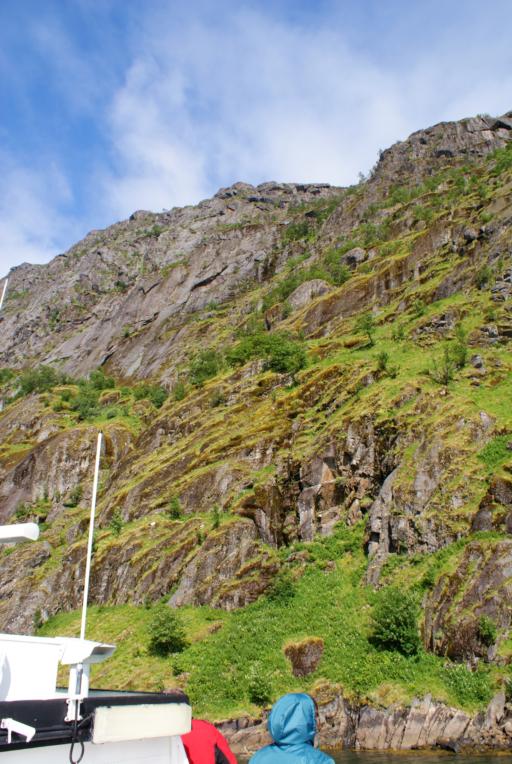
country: NO
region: Nordland
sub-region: Hadsel
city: Stokmarknes
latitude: 68.3642
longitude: 14.9812
